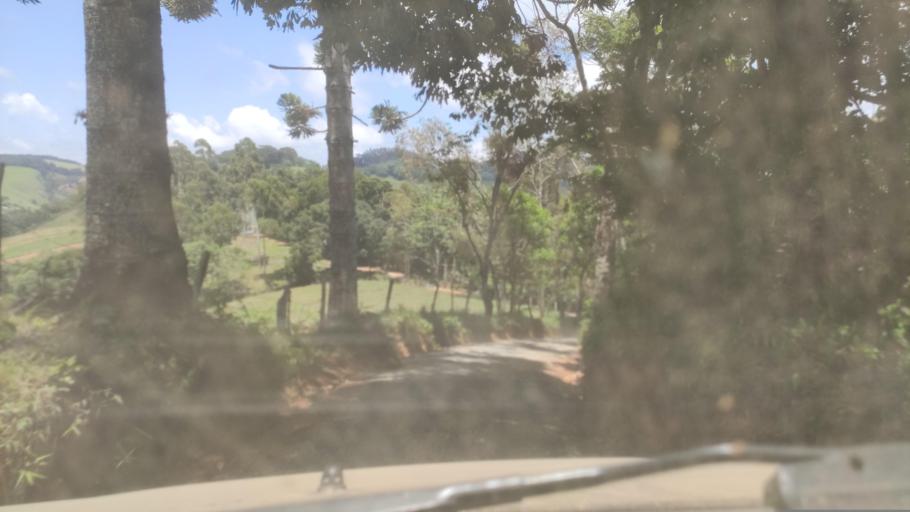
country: BR
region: Minas Gerais
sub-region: Cambui
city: Cambui
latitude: -22.6712
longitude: -45.9605
